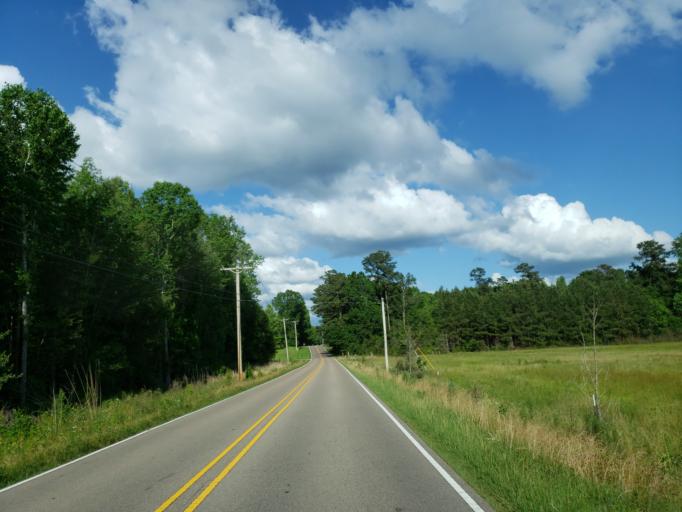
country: US
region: Mississippi
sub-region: Lamar County
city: West Hattiesburg
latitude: 31.2736
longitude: -89.3718
